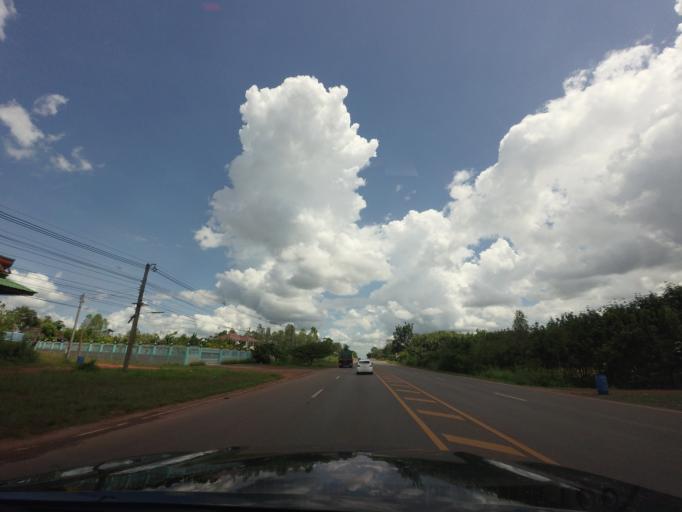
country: TH
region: Changwat Udon Thani
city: Ban Dung
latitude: 17.6849
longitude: 103.2088
